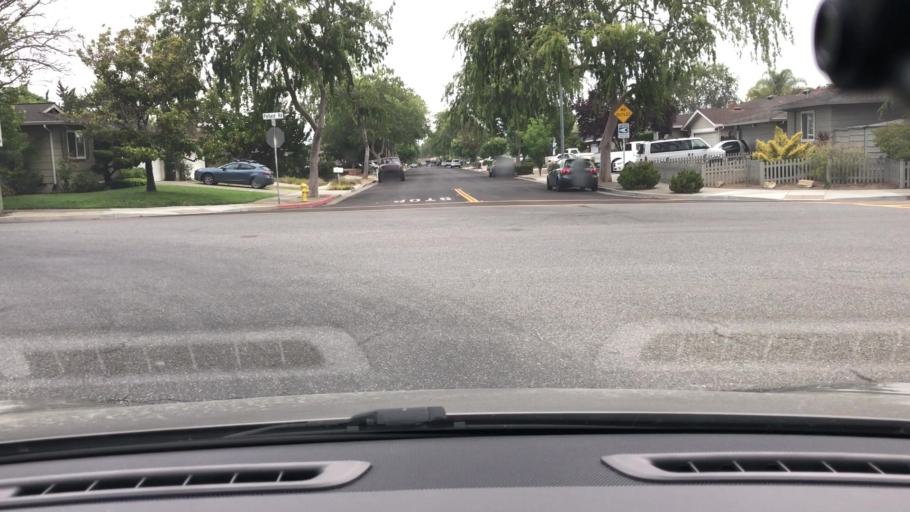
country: US
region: California
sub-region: Santa Clara County
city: Monte Sereno
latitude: 37.2636
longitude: -121.9883
